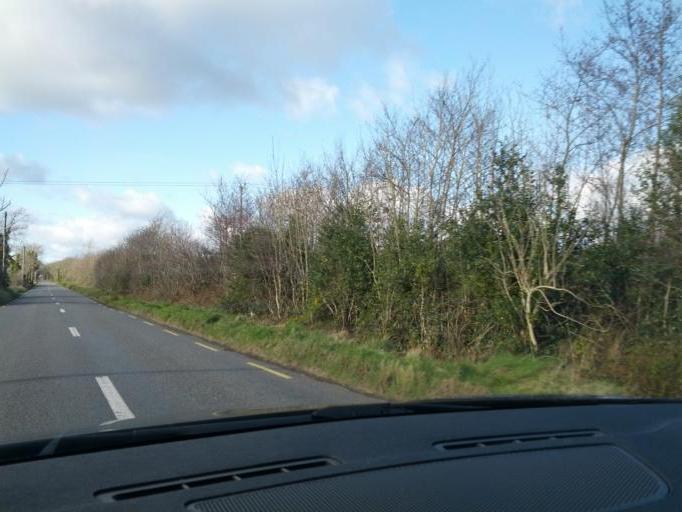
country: IE
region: Connaught
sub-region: County Galway
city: Athenry
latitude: 53.4945
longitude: -8.5674
